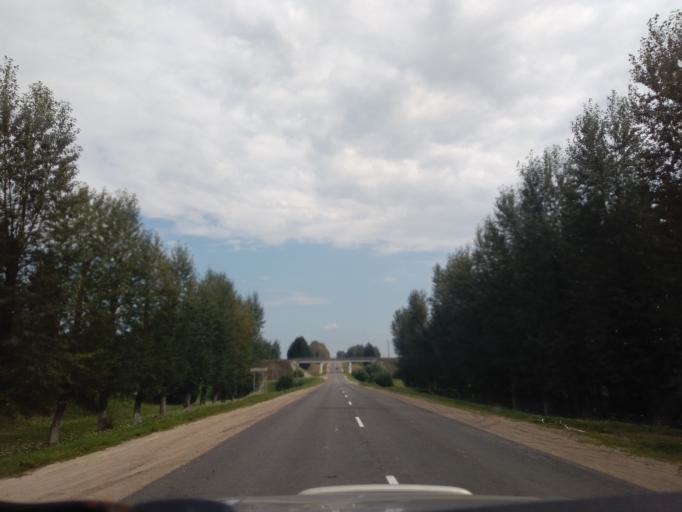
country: BY
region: Minsk
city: Khatsyezhyna
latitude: 53.9132
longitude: 27.3190
